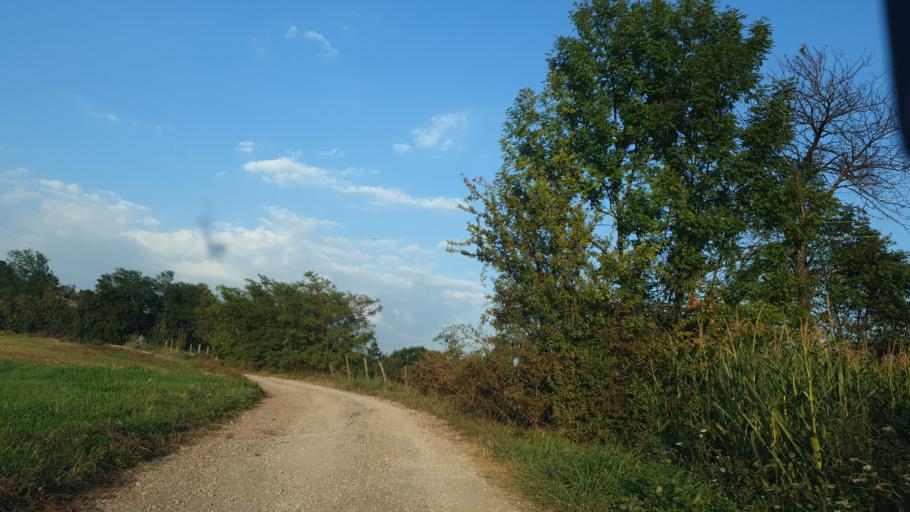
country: RS
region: Central Serbia
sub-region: Zlatiborski Okrug
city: Kosjeric
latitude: 43.9942
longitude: 20.0003
